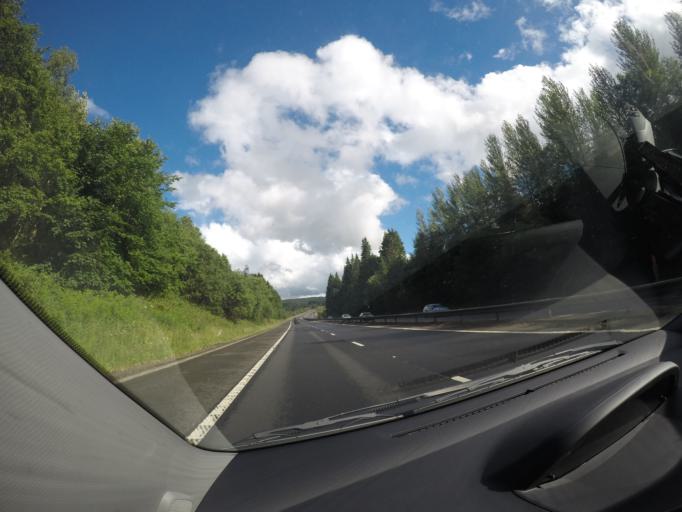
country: GB
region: Scotland
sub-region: South Lanarkshire
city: Douglas
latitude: 55.5806
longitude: -3.8202
